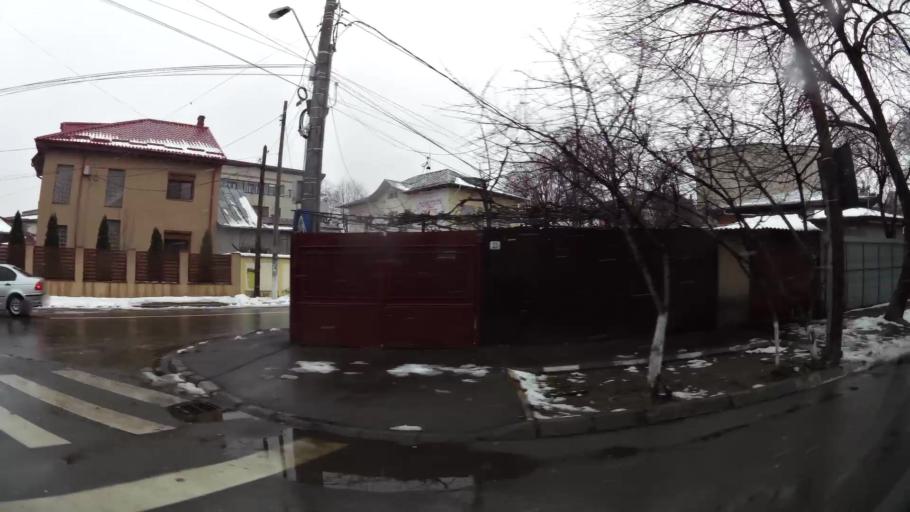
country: RO
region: Ilfov
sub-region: Comuna Chiajna
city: Rosu
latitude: 44.4894
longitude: 26.0431
